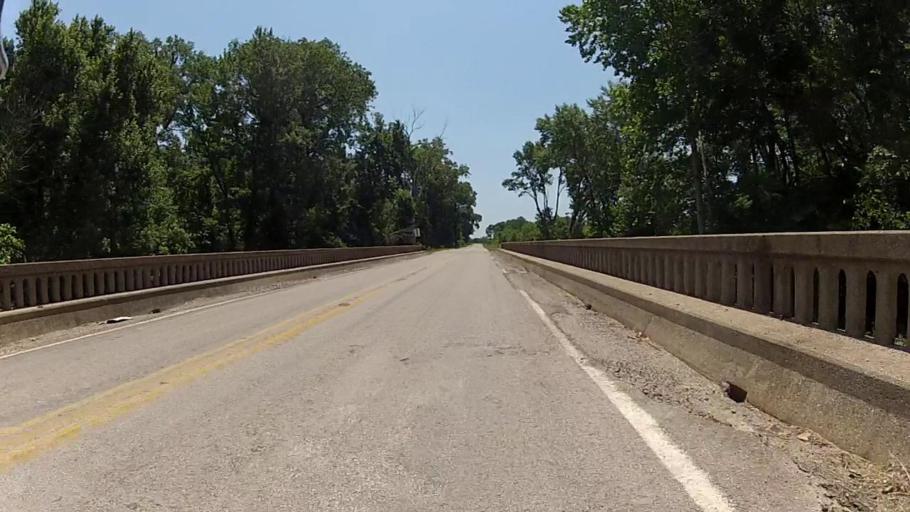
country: US
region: Kansas
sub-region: Montgomery County
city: Cherryvale
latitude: 37.2099
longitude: -95.5391
